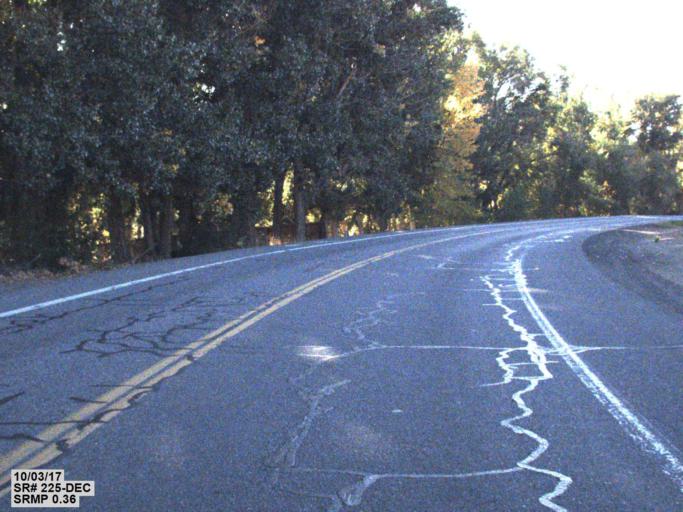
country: US
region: Washington
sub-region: Benton County
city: Benton City
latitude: 46.2571
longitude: -119.4760
